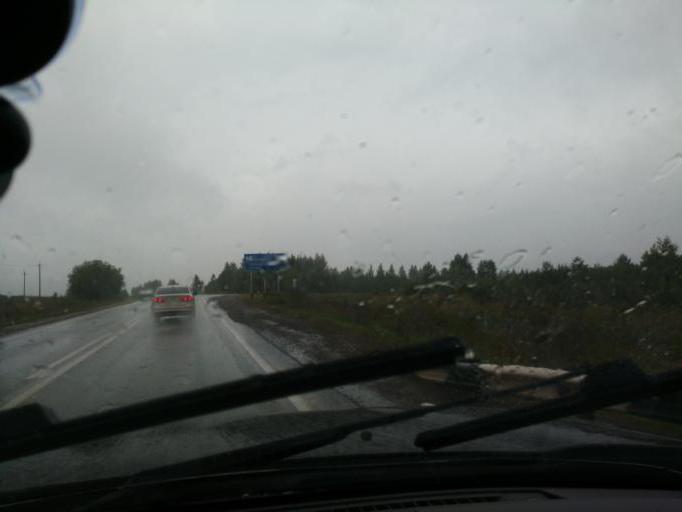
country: RU
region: Perm
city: Osa
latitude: 57.1772
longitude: 55.5317
